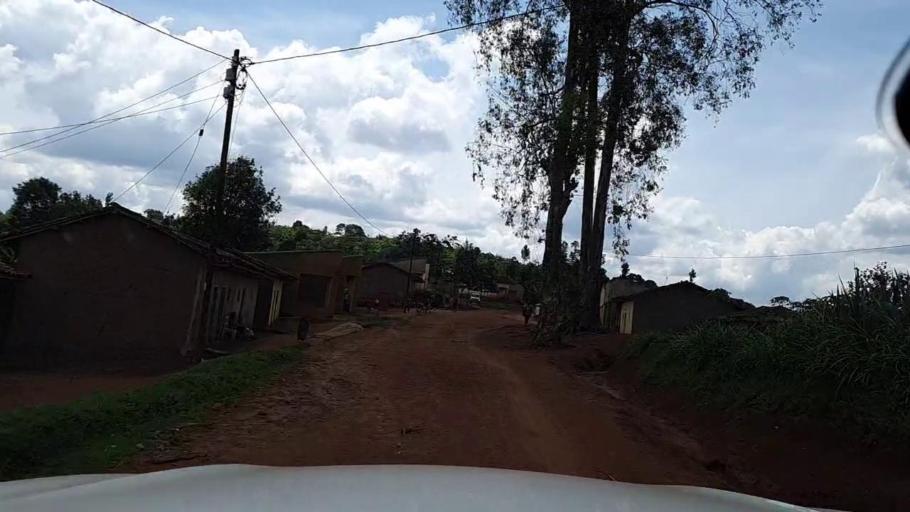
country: RW
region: Southern Province
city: Butare
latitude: -2.7612
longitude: 29.7441
